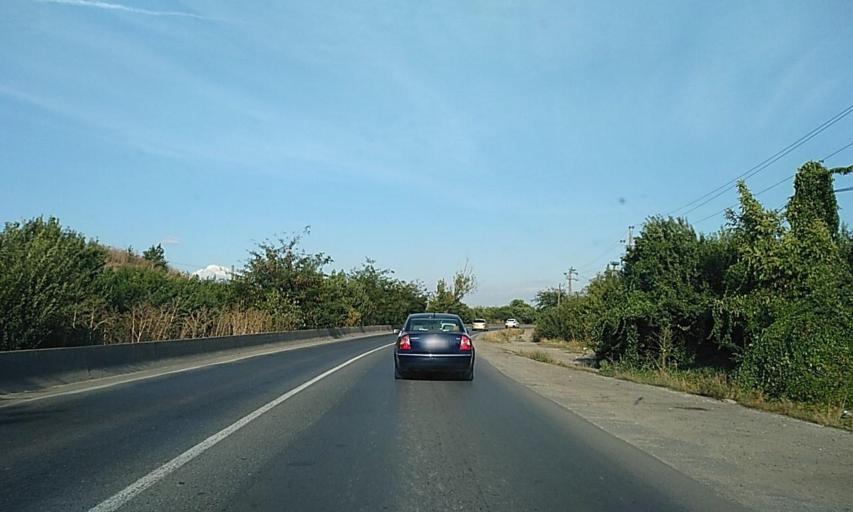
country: RO
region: Ilfov
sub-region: Comuna Glina
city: Catelu
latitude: 44.3766
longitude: 26.2194
